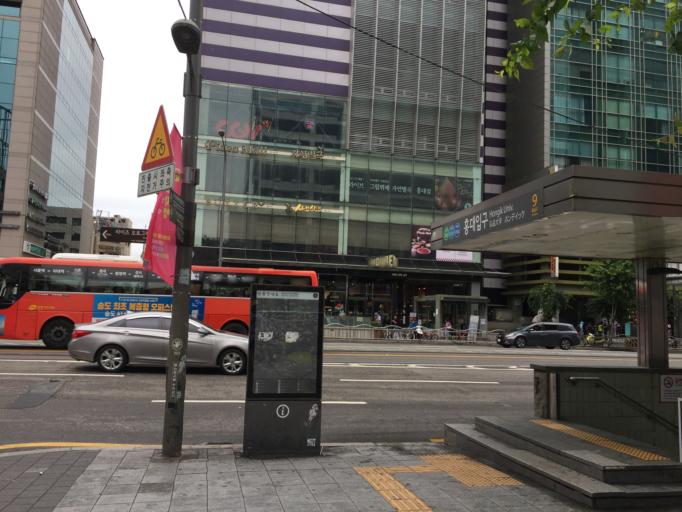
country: KR
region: Seoul
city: Seoul
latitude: 37.5561
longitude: 126.9230
